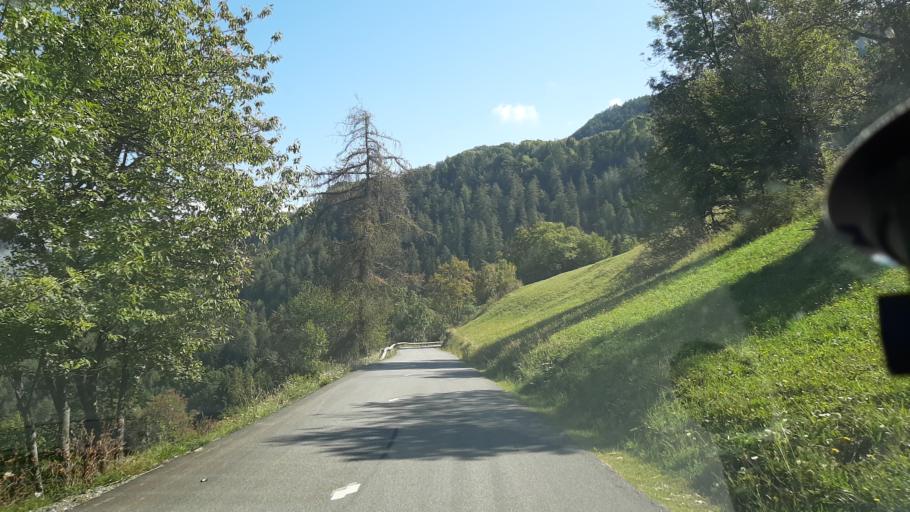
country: FR
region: Rhone-Alpes
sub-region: Departement de la Savoie
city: Aime
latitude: 45.5190
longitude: 6.5953
